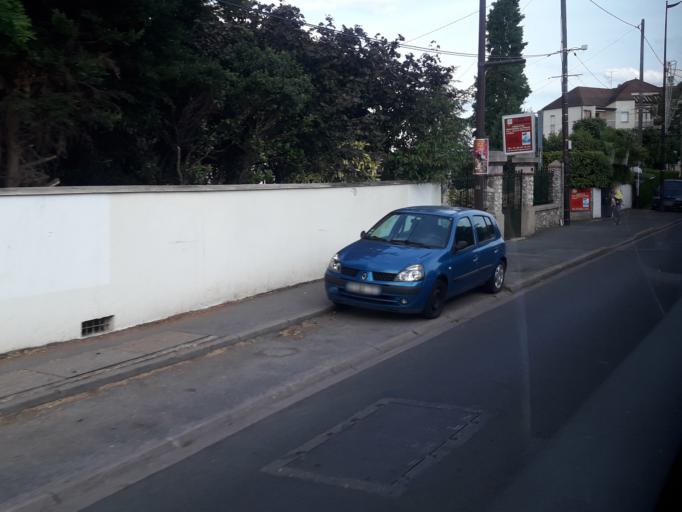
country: FR
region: Ile-de-France
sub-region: Departement de l'Essonne
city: Epinay-sur-Orge
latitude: 48.6768
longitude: 2.3211
